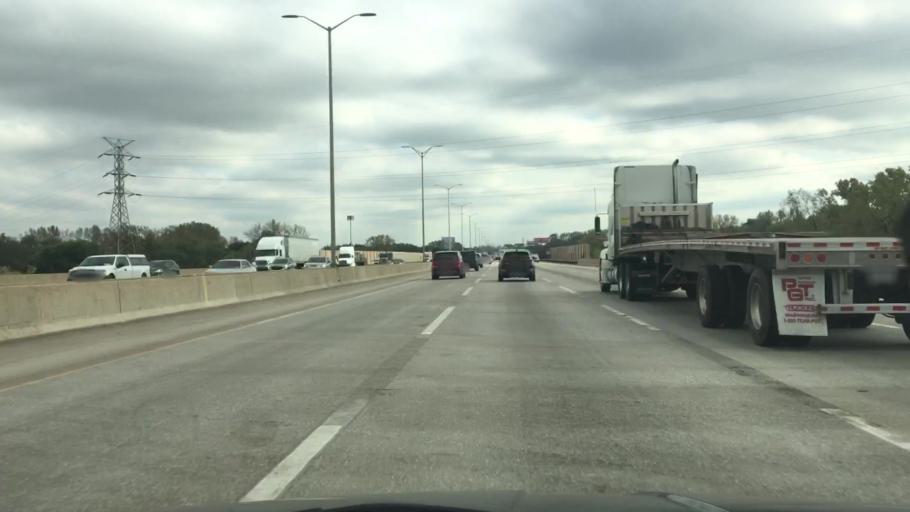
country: US
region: Illinois
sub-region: Cook County
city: Alsip
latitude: 41.6520
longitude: -87.7254
